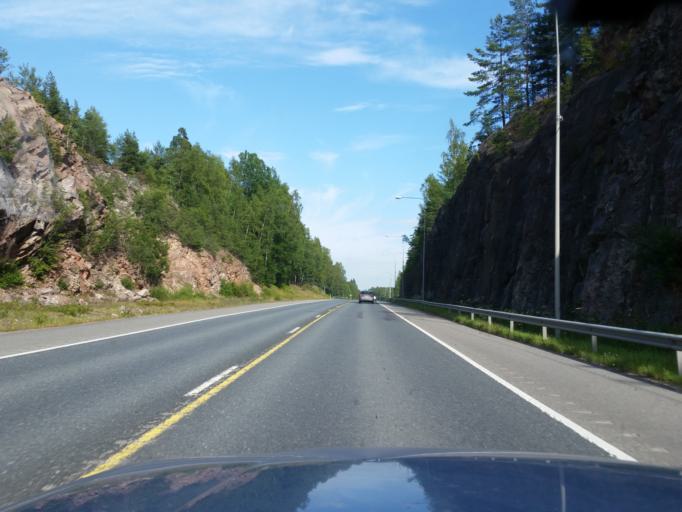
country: FI
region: Uusimaa
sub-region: Helsinki
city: Siuntio
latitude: 60.0964
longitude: 24.2633
